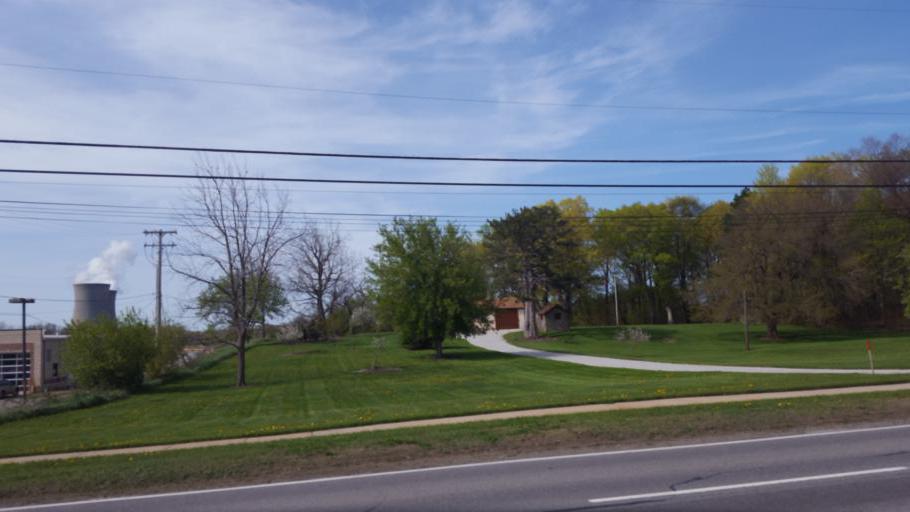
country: US
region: Ohio
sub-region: Lake County
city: Perry
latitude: 41.7859
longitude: -81.1310
